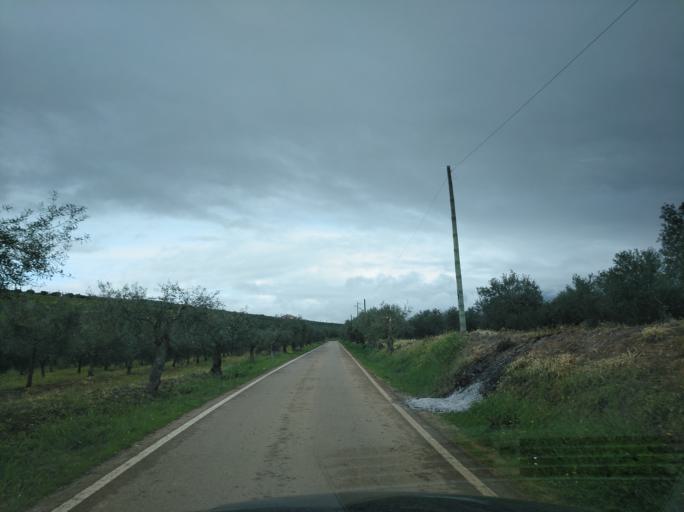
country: PT
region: Portalegre
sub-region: Campo Maior
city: Campo Maior
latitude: 38.9972
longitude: -7.0513
